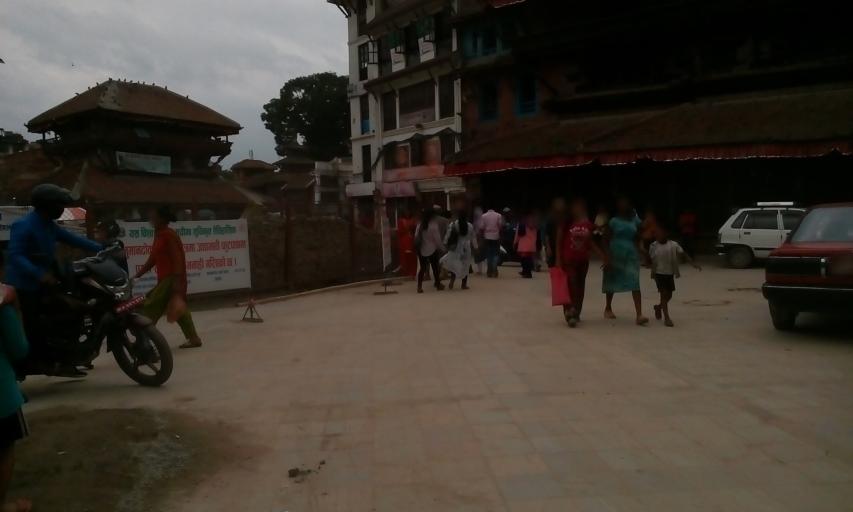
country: NP
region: Central Region
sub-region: Bagmati Zone
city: Kathmandu
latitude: 27.7038
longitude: 85.3057
